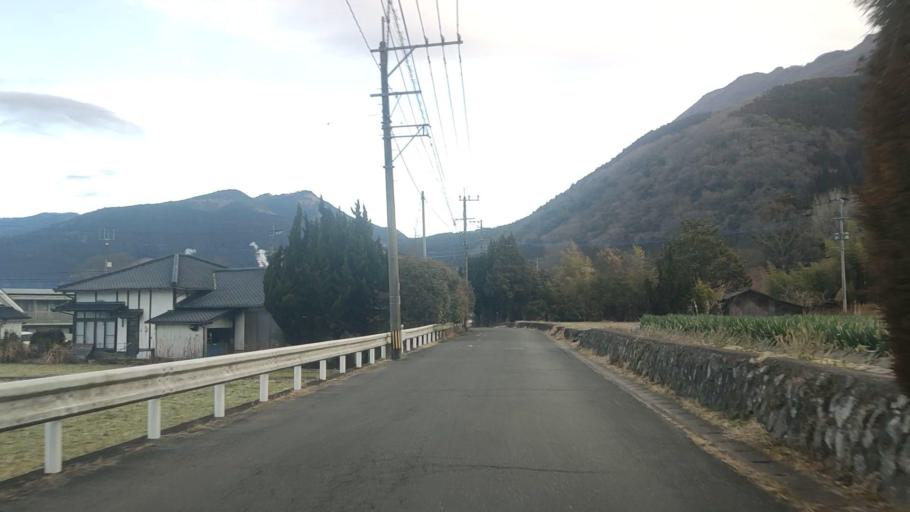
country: JP
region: Oita
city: Beppu
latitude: 33.2607
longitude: 131.3686
